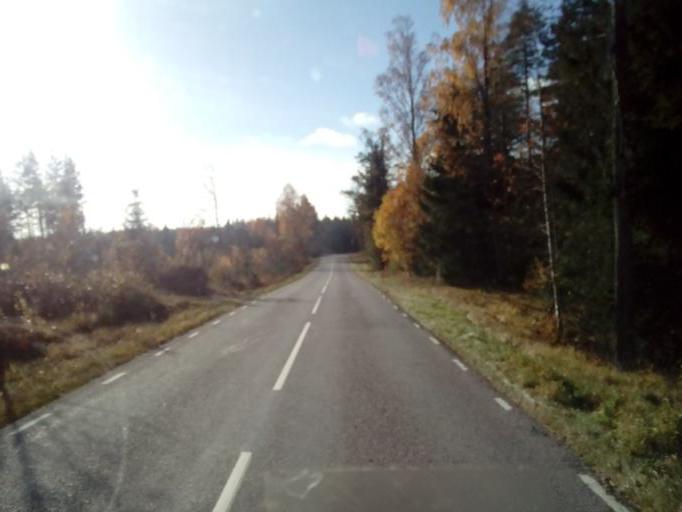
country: SE
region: Kalmar
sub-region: Vasterviks Kommun
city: Ankarsrum
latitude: 57.7649
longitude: 16.1363
